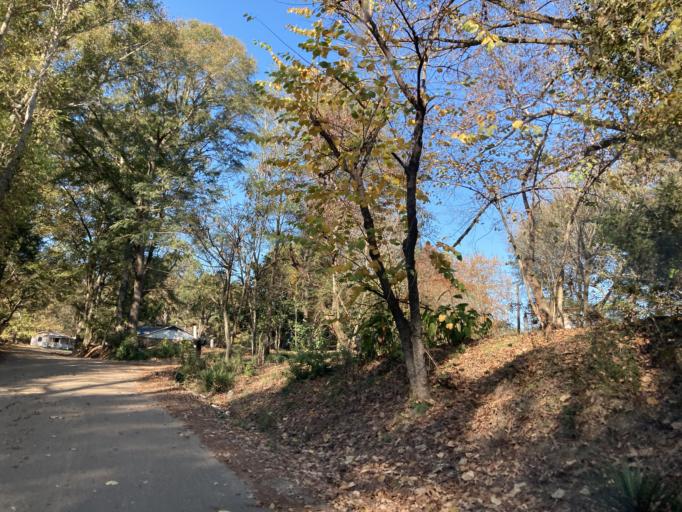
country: US
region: Mississippi
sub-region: Yazoo County
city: Yazoo City
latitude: 32.7603
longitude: -90.2765
